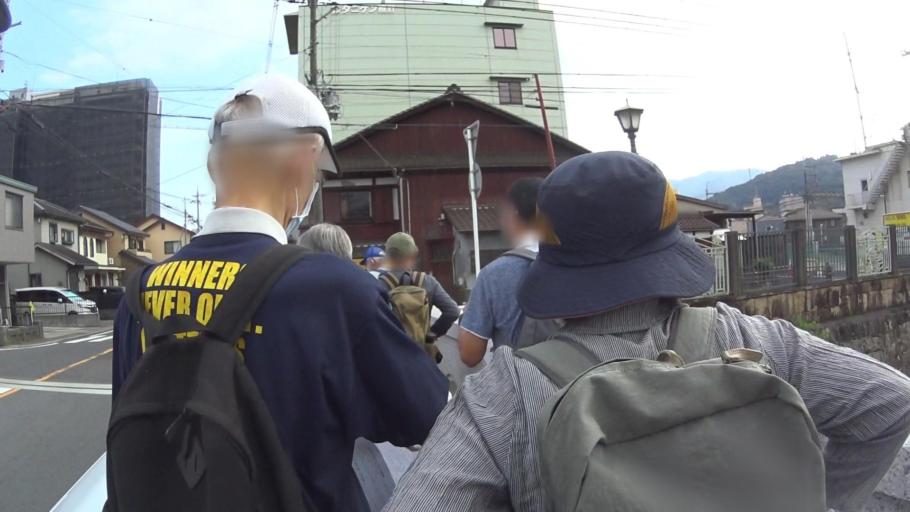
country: JP
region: Shiga Prefecture
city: Nagahama
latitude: 35.3912
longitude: 136.2302
